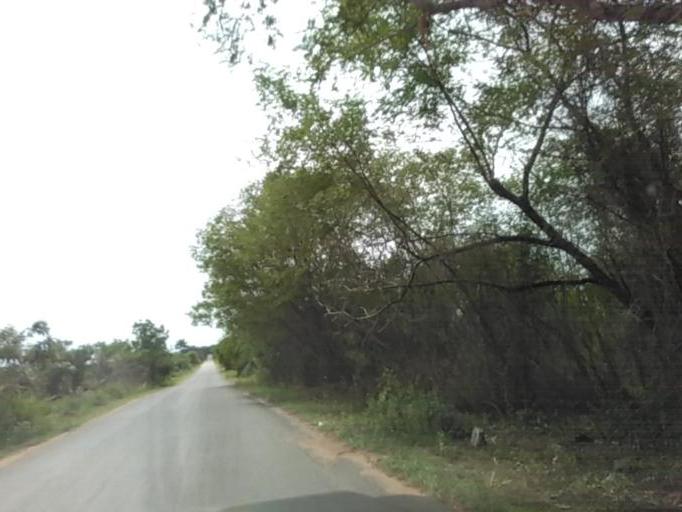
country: GH
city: Akropong
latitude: 6.0928
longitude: 0.0697
